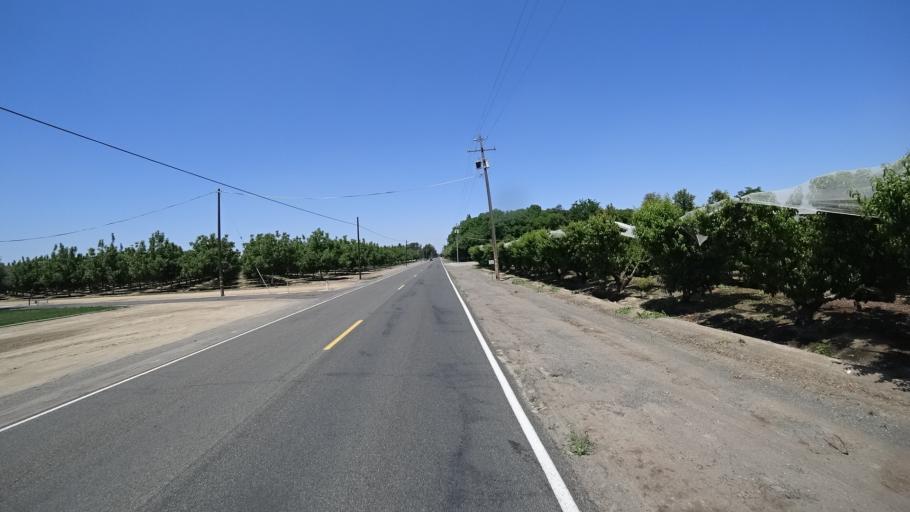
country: US
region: California
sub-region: Kings County
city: Lucerne
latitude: 36.3891
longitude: -119.6550
